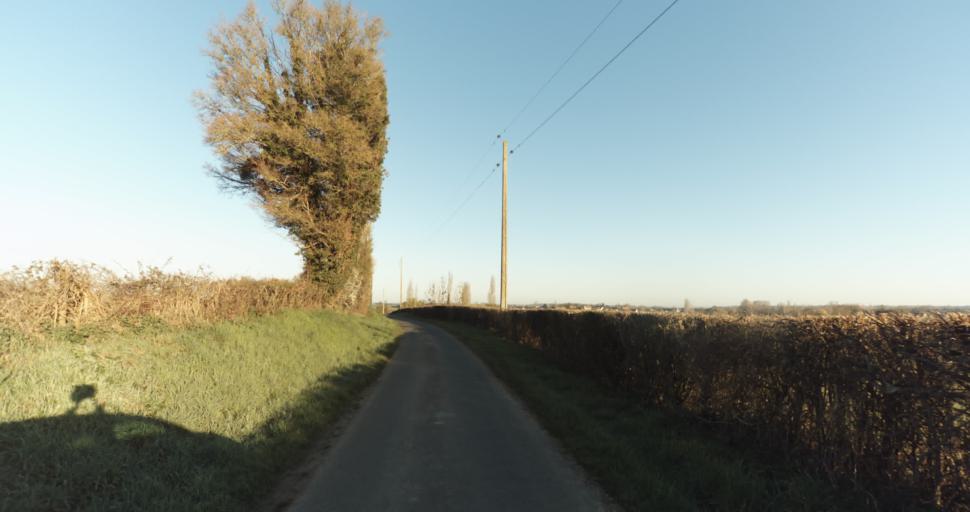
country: FR
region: Lower Normandy
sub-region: Departement du Calvados
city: Saint-Pierre-sur-Dives
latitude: 49.0285
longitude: -0.0215
